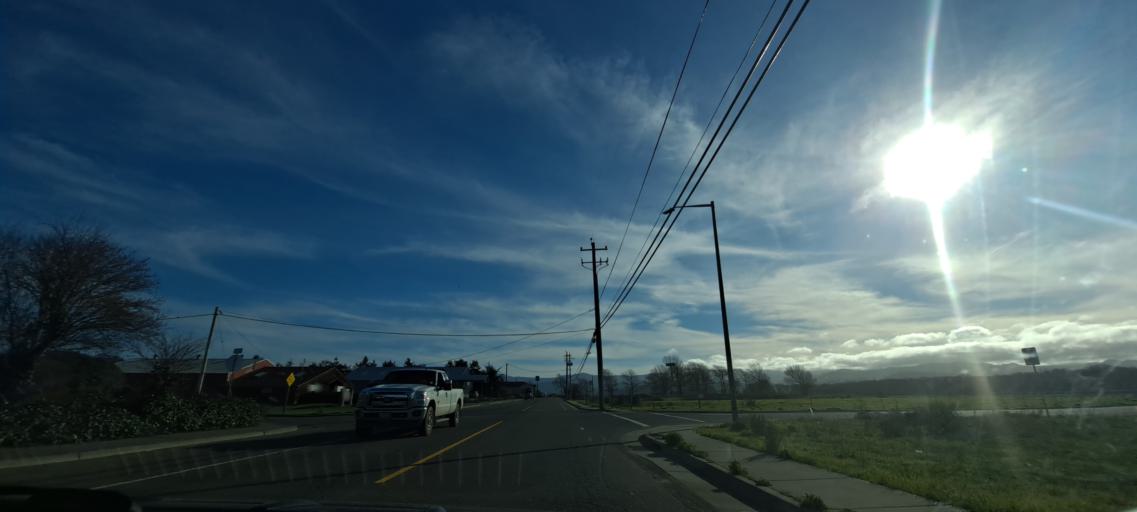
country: US
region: California
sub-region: Humboldt County
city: Fortuna
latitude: 40.5825
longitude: -124.1547
